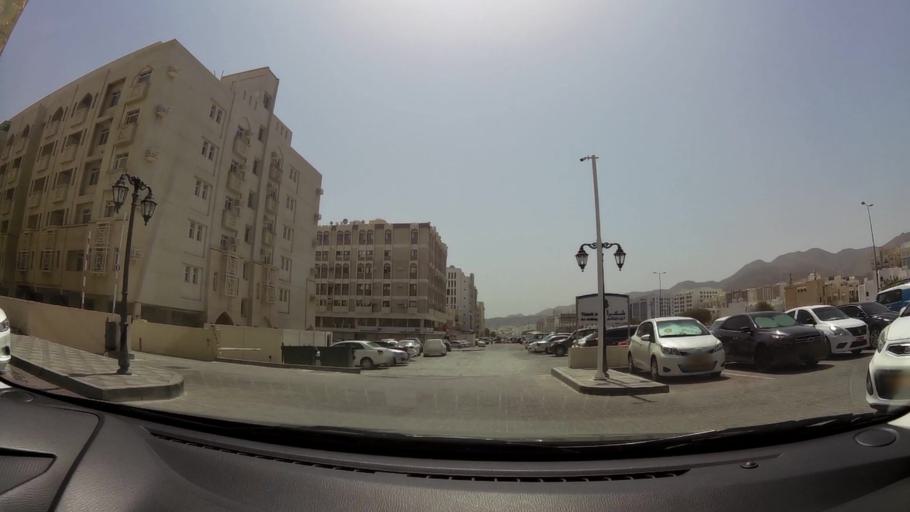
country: OM
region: Muhafazat Masqat
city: Bawshar
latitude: 23.5854
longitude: 58.4221
